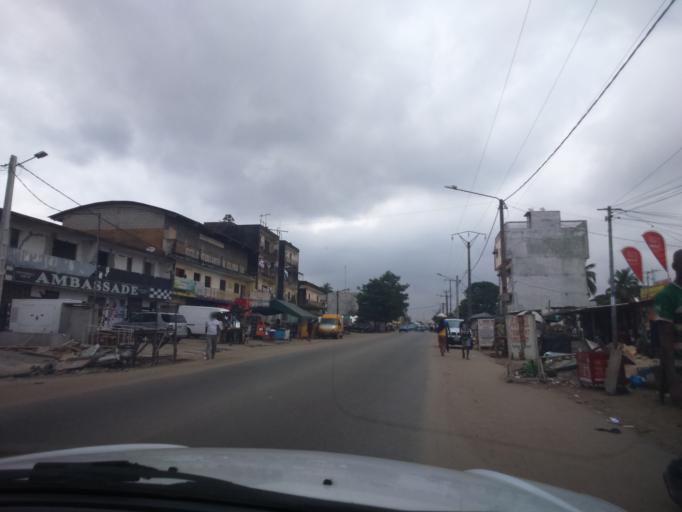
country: CI
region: Lagunes
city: Abidjan
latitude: 5.3466
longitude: -4.0671
